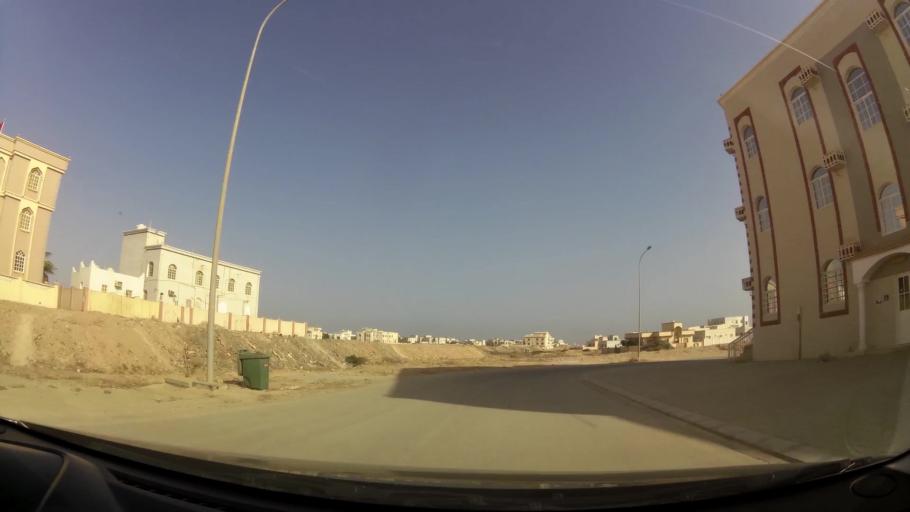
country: OM
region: Zufar
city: Salalah
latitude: 17.0083
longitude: 54.0256
